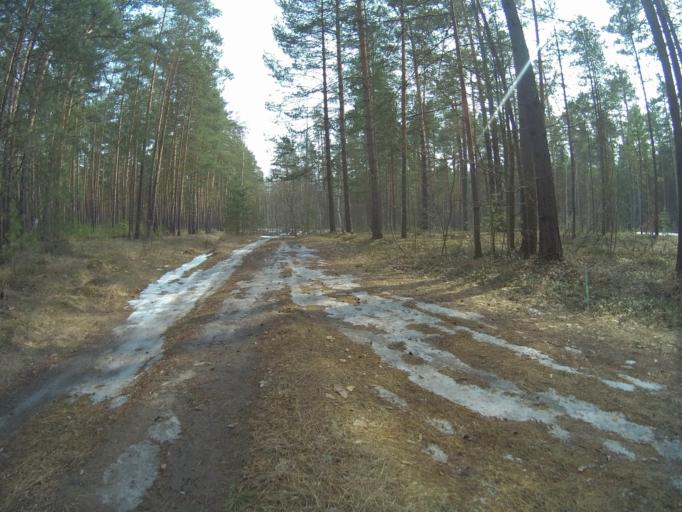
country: RU
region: Vladimir
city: Raduzhnyy
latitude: 56.0333
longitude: 40.3742
